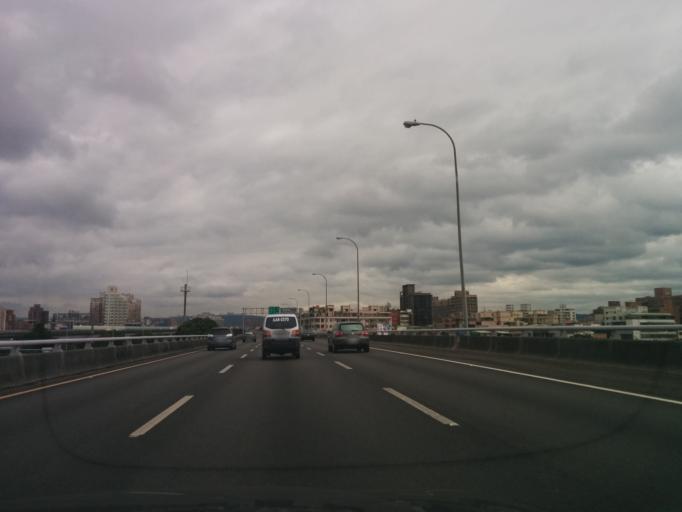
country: TW
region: Taipei
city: Taipei
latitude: 25.0768
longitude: 121.4967
